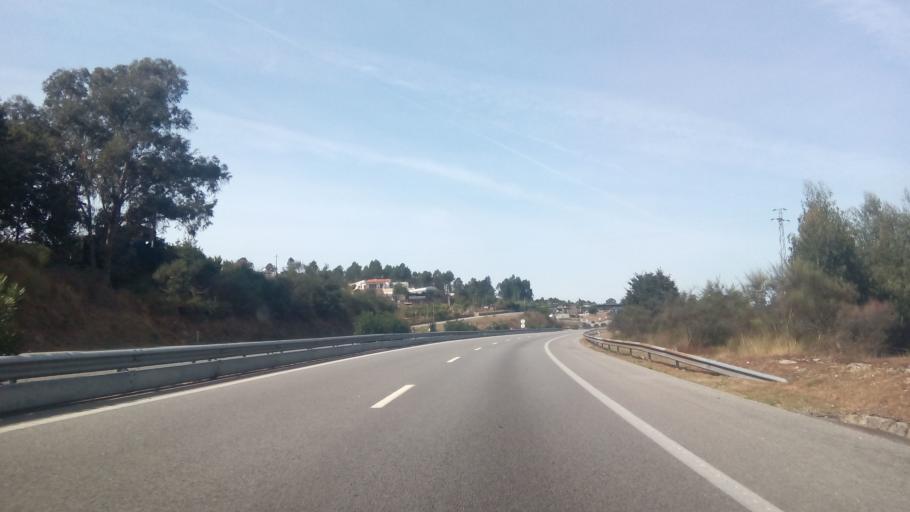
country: PT
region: Porto
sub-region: Marco de Canaveses
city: Marco de Canavezes
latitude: 41.2278
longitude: -8.1747
